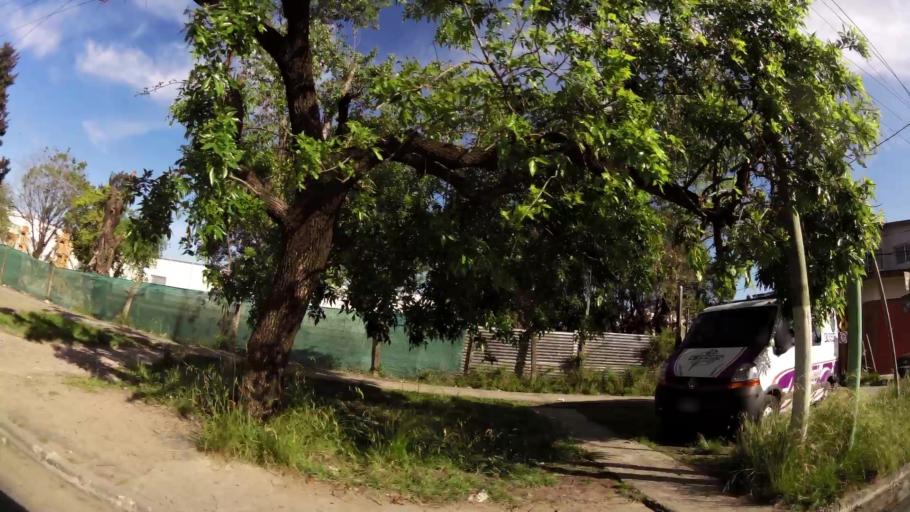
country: AR
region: Buenos Aires
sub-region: Partido de Quilmes
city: Quilmes
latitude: -34.7860
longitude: -58.2373
